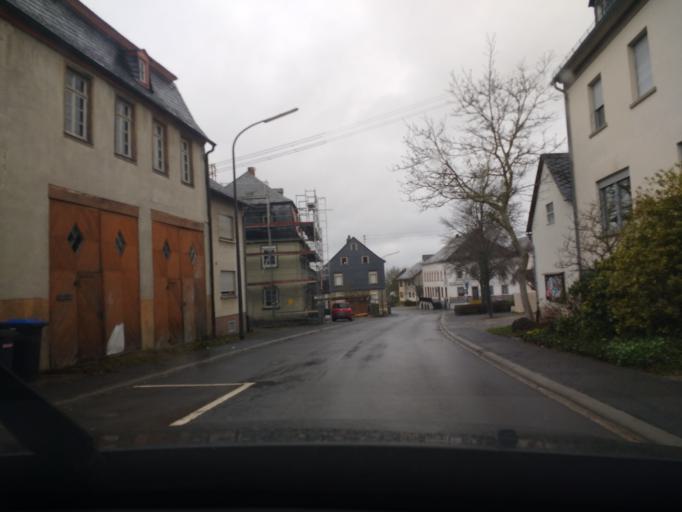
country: DE
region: Rheinland-Pfalz
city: Irmenach
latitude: 49.9236
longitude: 7.1880
